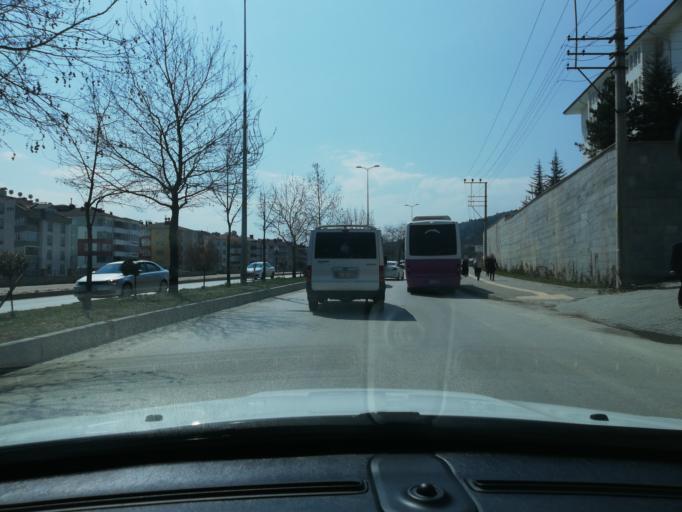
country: TR
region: Kastamonu
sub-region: Cide
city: Kastamonu
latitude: 41.4028
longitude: 33.7831
